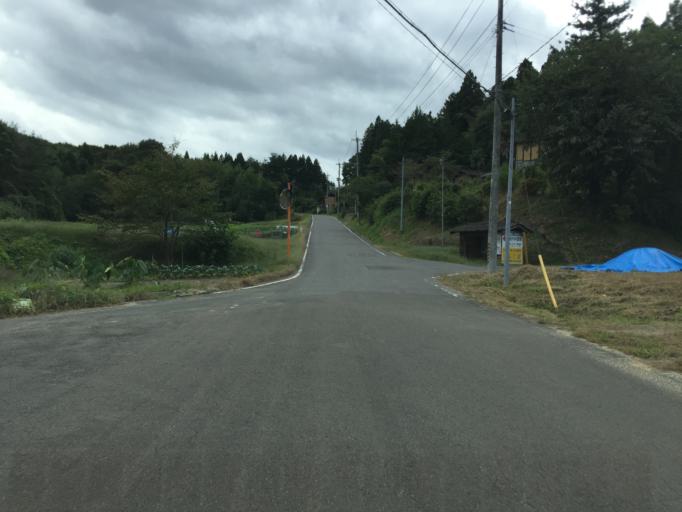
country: JP
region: Fukushima
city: Fukushima-shi
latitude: 37.6907
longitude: 140.4898
